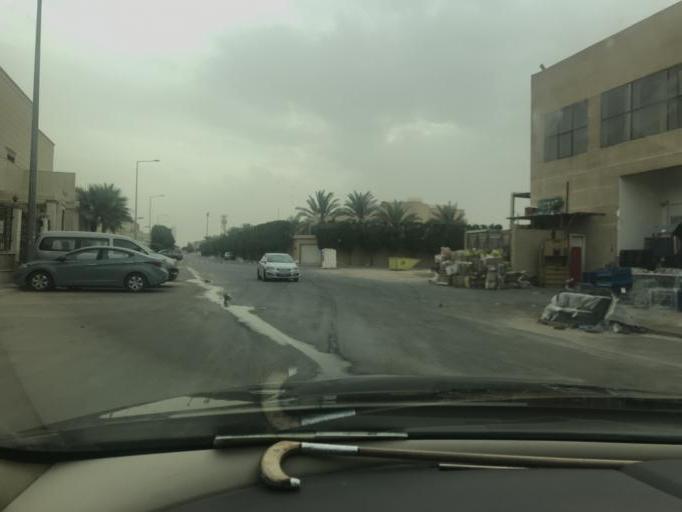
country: SA
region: Ar Riyad
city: Riyadh
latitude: 24.7890
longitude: 46.7019
